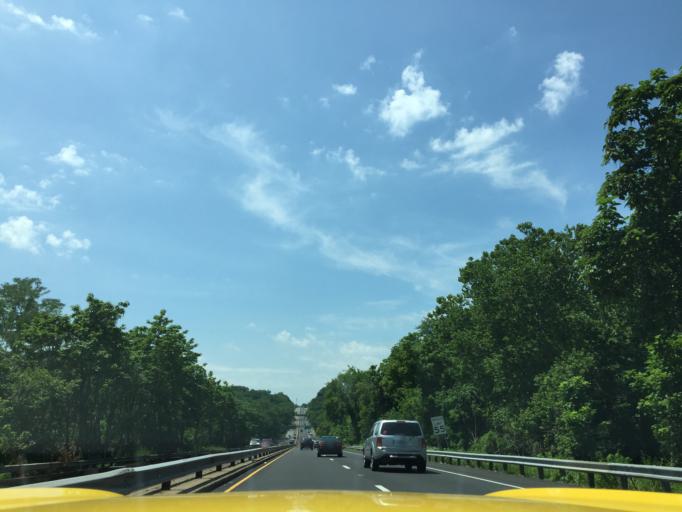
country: US
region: Pennsylvania
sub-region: Bucks County
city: Trevose
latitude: 40.1496
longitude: -74.9501
